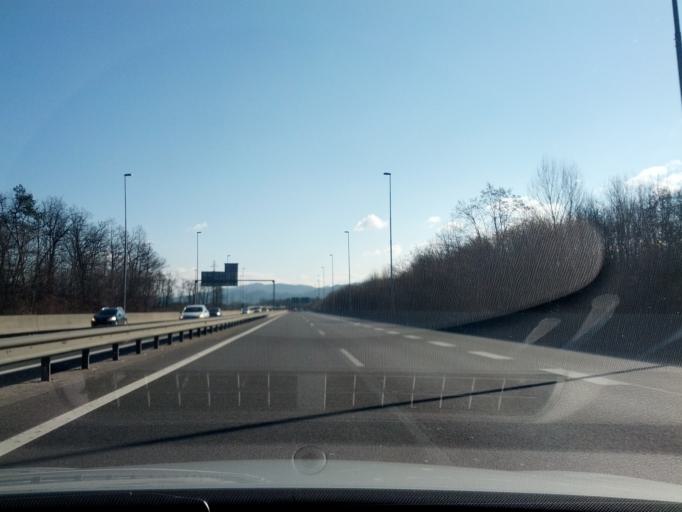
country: SI
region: Dol pri Ljubljani
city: Dol pri Ljubljani
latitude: 46.0674
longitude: 14.5633
